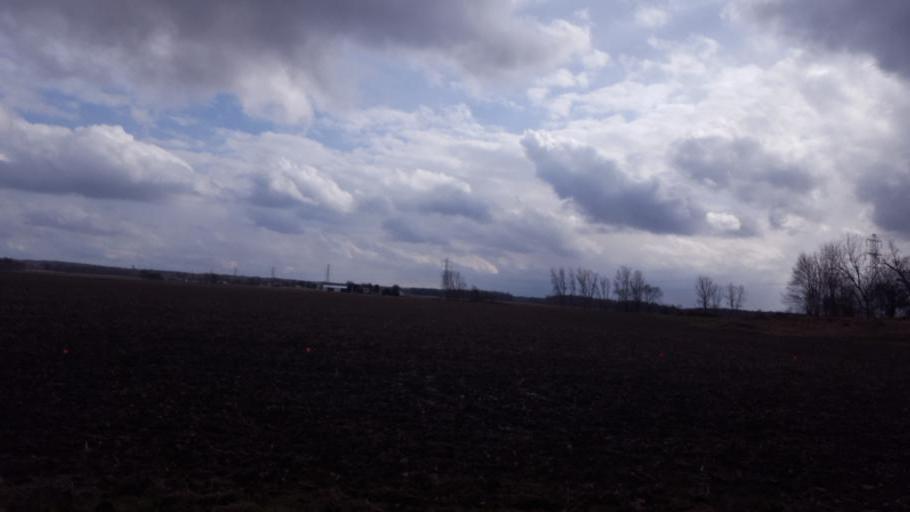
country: US
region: Ohio
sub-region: Richland County
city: Shelby
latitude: 40.8284
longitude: -82.6609
